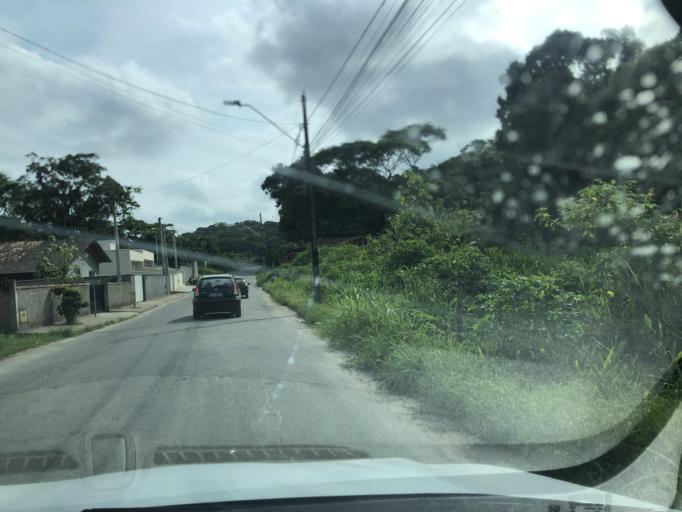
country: BR
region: Santa Catarina
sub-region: Sao Francisco Do Sul
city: Sao Francisco do Sul
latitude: -26.2287
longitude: -48.6052
